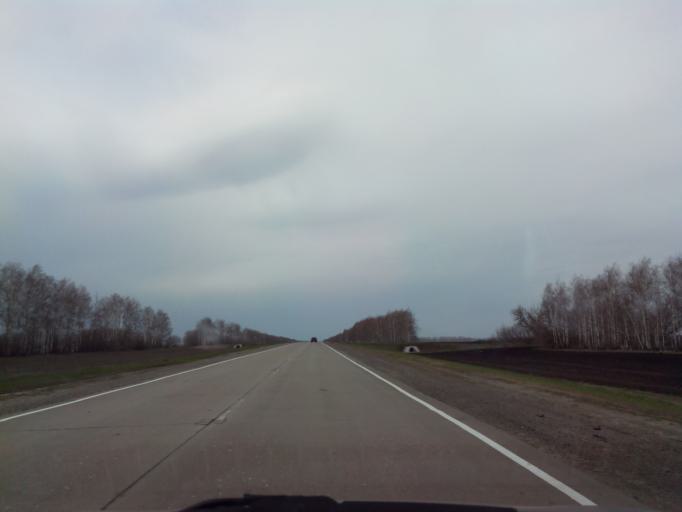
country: RU
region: Tambov
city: Znamenka
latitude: 52.2606
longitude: 41.5057
